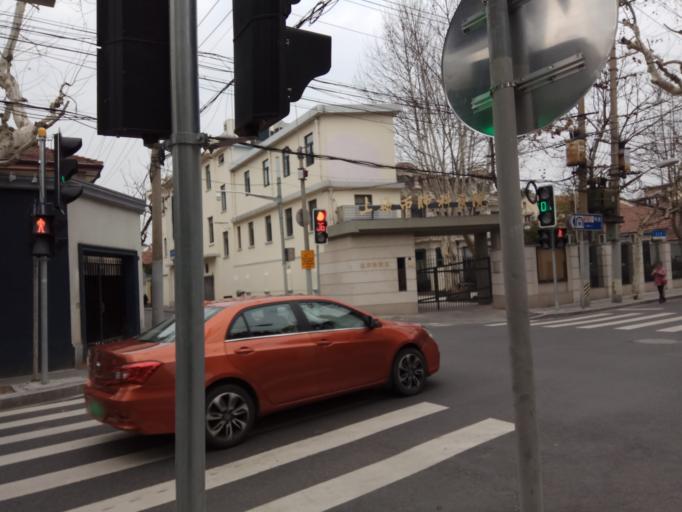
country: CN
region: Shanghai Shi
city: Shanghai
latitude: 31.2167
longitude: 121.4455
